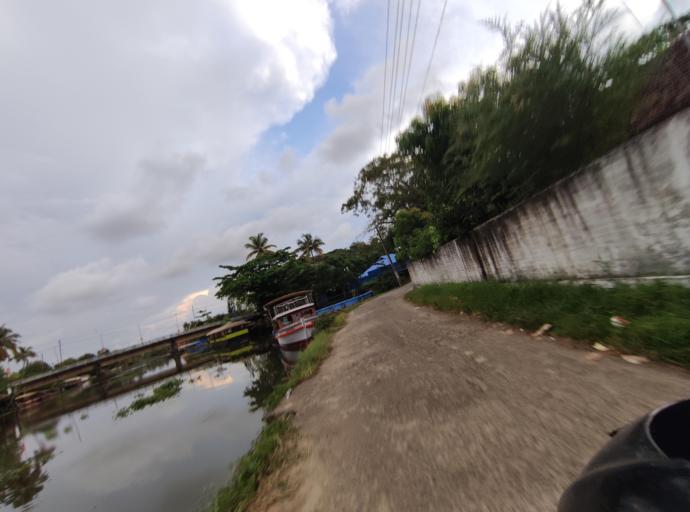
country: IN
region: Kerala
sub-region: Alappuzha
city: Shertallai
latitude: 9.6287
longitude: 76.4289
